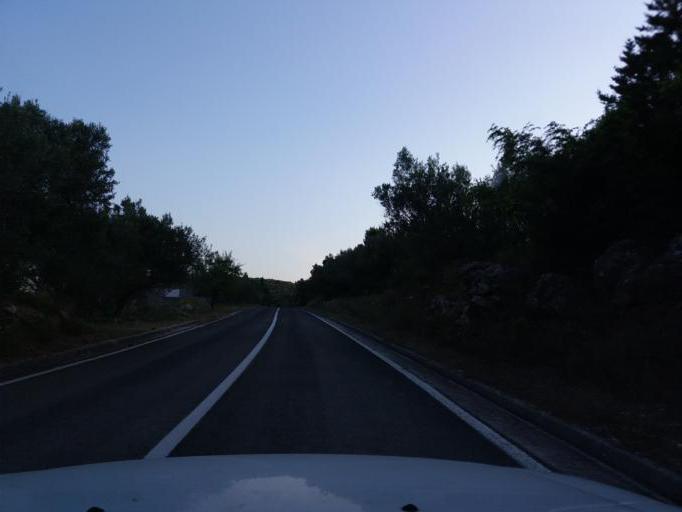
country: HR
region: Zadarska
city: Ugljan
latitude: 44.0798
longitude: 15.0015
